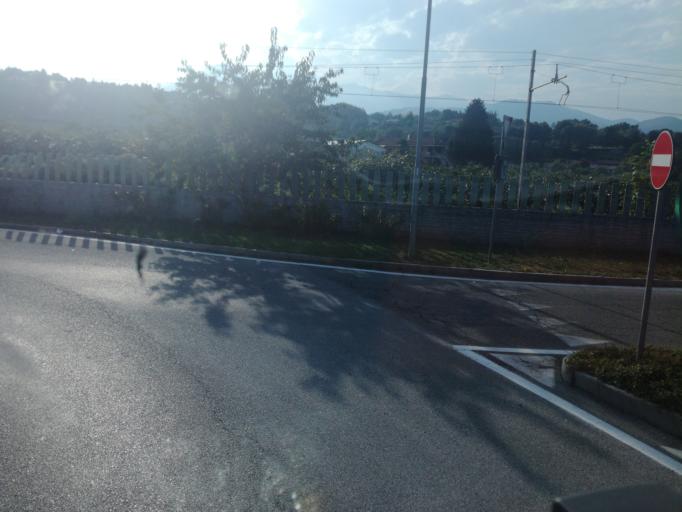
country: IT
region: Piedmont
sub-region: Provincia di Torino
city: Bricherasio
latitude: 44.8145
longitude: 7.2960
